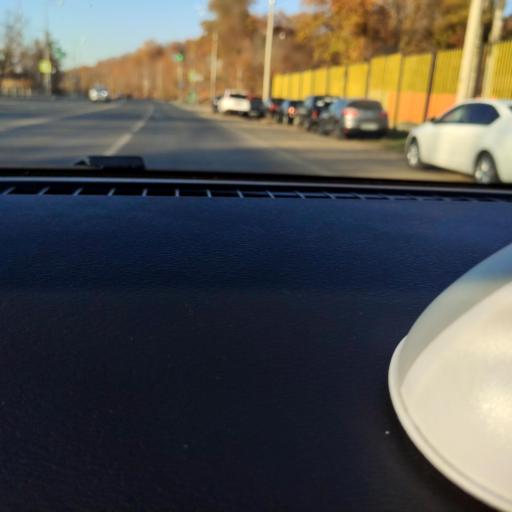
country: RU
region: Samara
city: Samara
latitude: 53.2790
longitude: 50.2290
